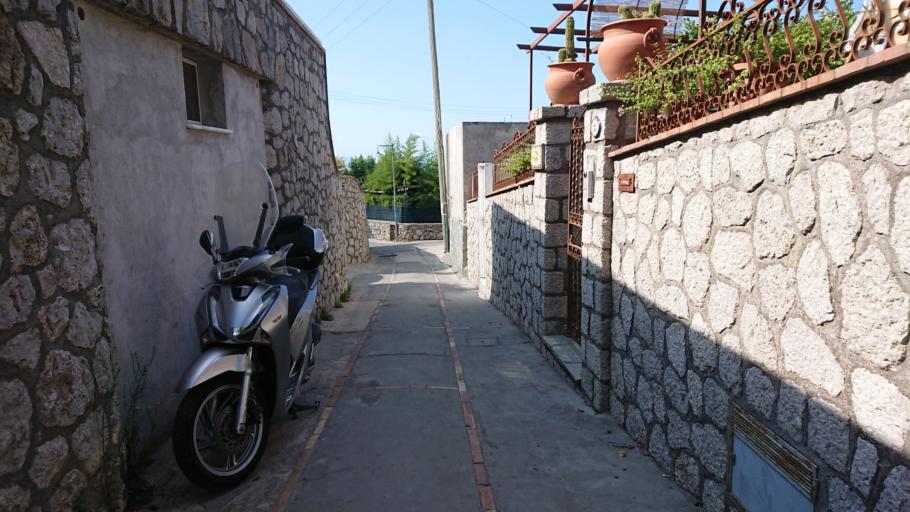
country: IT
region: Campania
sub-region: Provincia di Napoli
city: Anacapri
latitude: 40.5555
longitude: 14.2152
